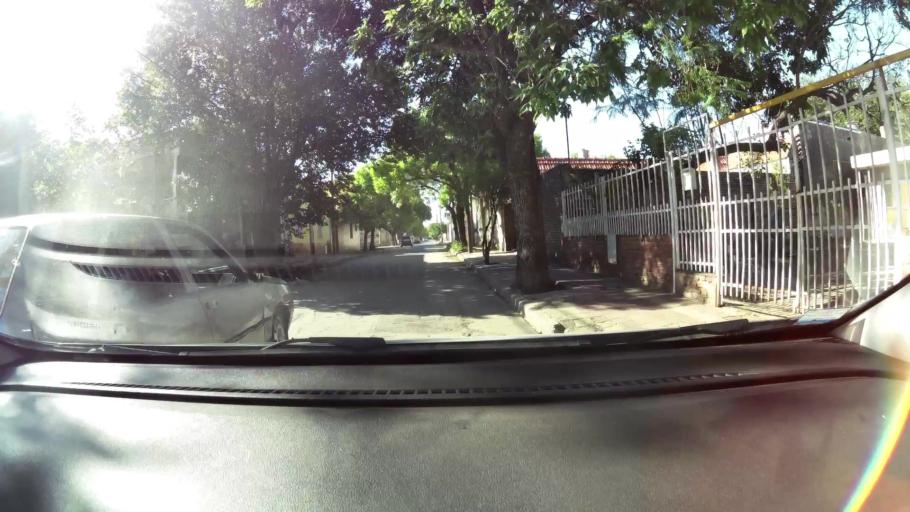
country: AR
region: Cordoba
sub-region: Departamento de Capital
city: Cordoba
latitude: -31.3987
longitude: -64.1533
